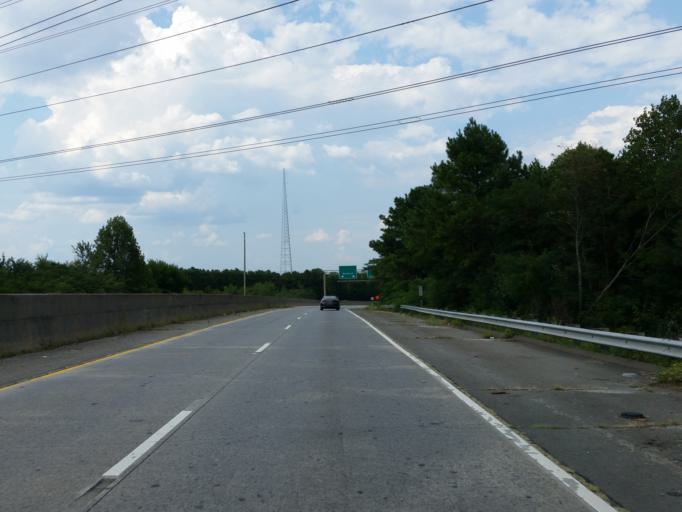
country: US
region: Georgia
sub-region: Cobb County
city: Marietta
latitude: 33.9759
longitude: -84.5498
